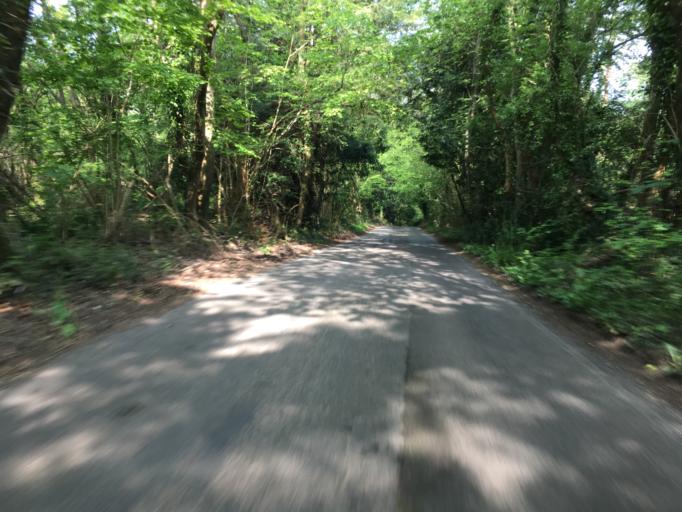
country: GB
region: England
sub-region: North Somerset
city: Nailsea
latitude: 51.4075
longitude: -2.7247
